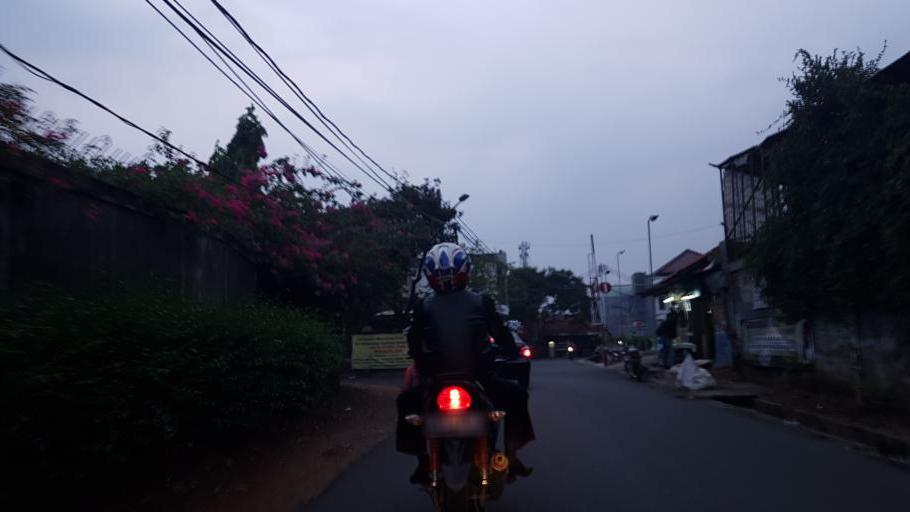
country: ID
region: West Java
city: Depok
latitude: -6.3645
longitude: 106.7985
